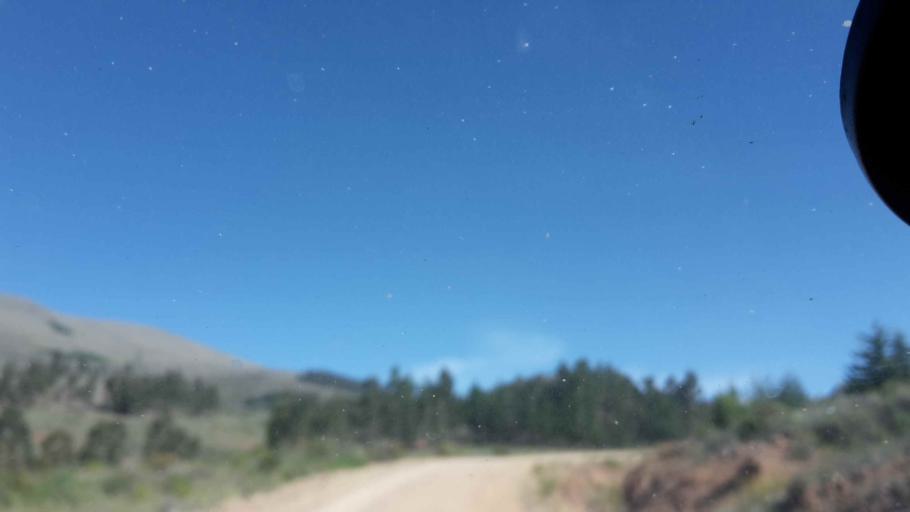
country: BO
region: Cochabamba
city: Arani
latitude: -17.6550
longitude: -65.7391
